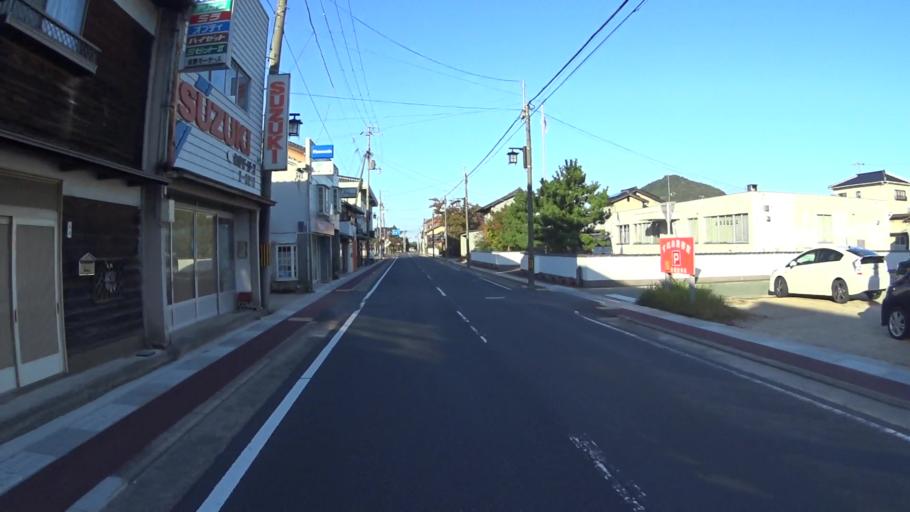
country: JP
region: Hyogo
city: Toyooka
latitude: 35.6050
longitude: 134.8957
